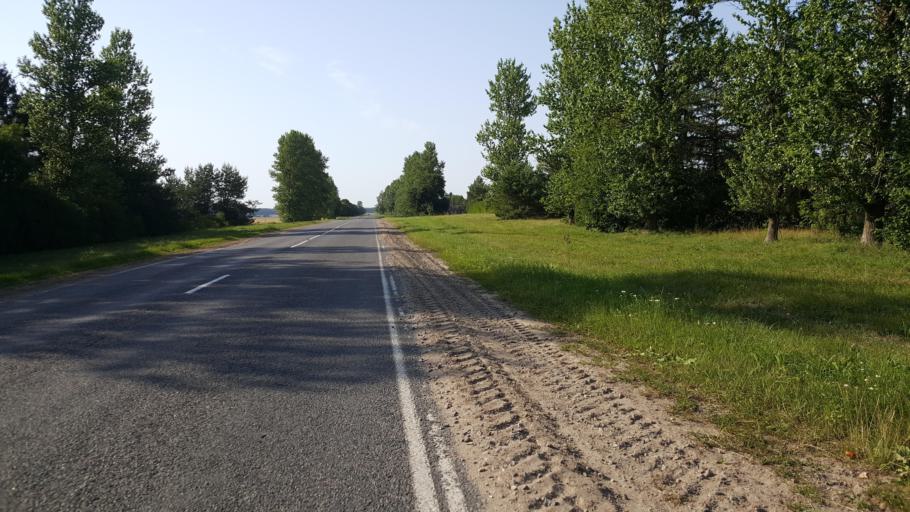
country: BY
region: Brest
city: Kamyanyets
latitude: 52.3536
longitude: 23.8973
